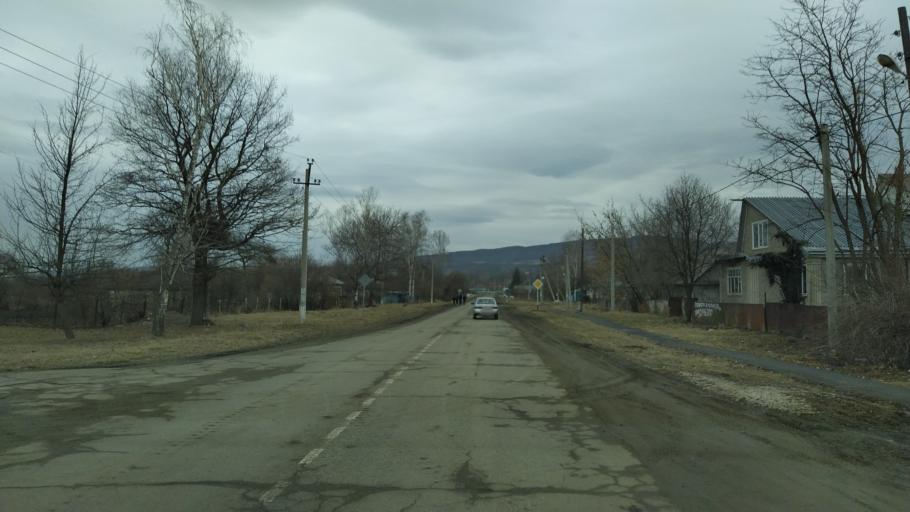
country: RU
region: Krasnodarskiy
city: Peredovaya
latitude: 44.1179
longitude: 41.4673
